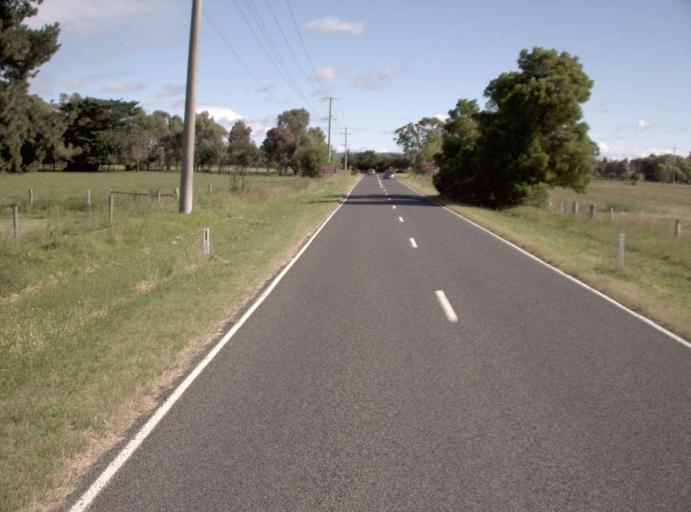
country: AU
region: Victoria
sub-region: Latrobe
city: Traralgon
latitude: -38.1801
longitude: 146.5002
